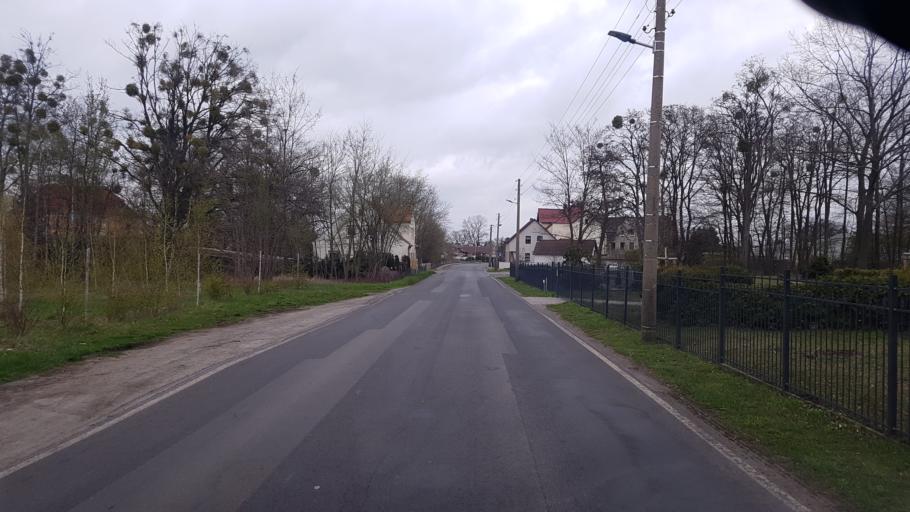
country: DE
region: Brandenburg
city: Hohenbocka
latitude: 51.4518
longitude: 14.0212
